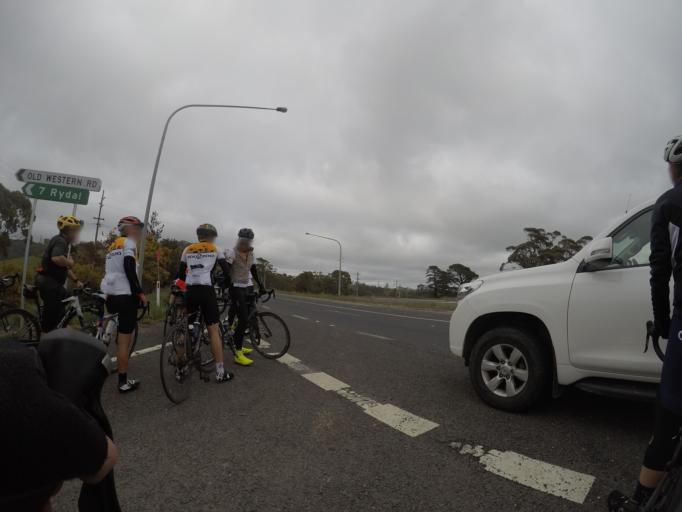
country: AU
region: New South Wales
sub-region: Lithgow
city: Portland
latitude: -33.4532
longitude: 149.9881
